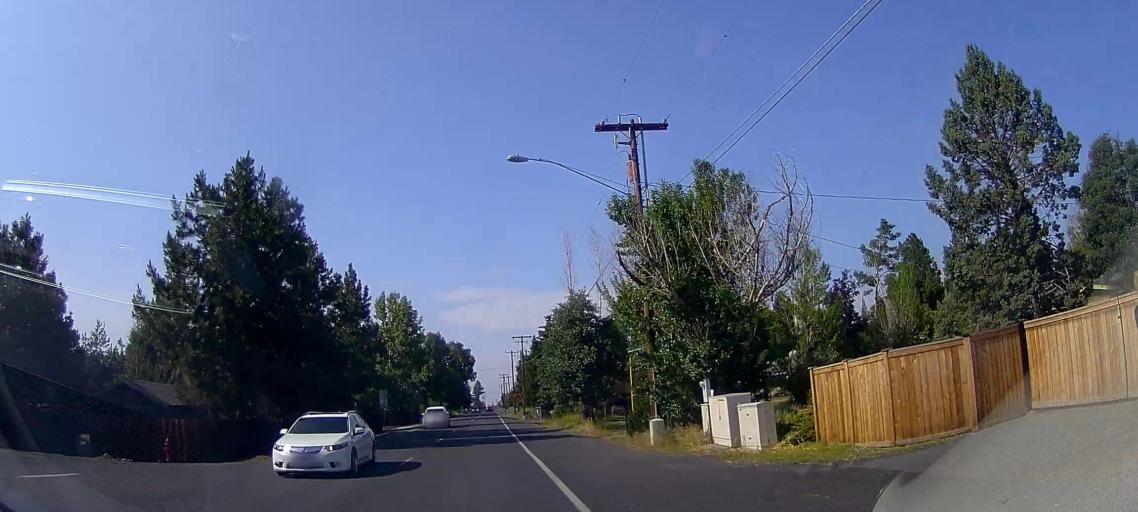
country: US
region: Oregon
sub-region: Deschutes County
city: Bend
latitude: 44.0492
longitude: -121.2686
